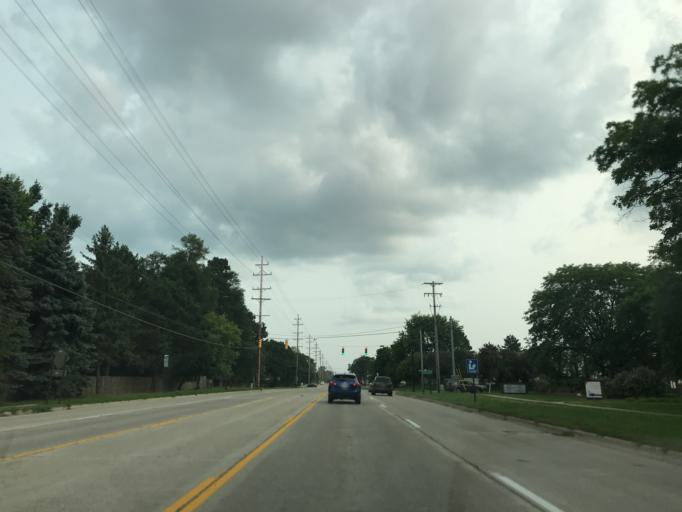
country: US
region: Michigan
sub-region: Ingham County
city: Okemos
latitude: 42.7078
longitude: -84.4324
